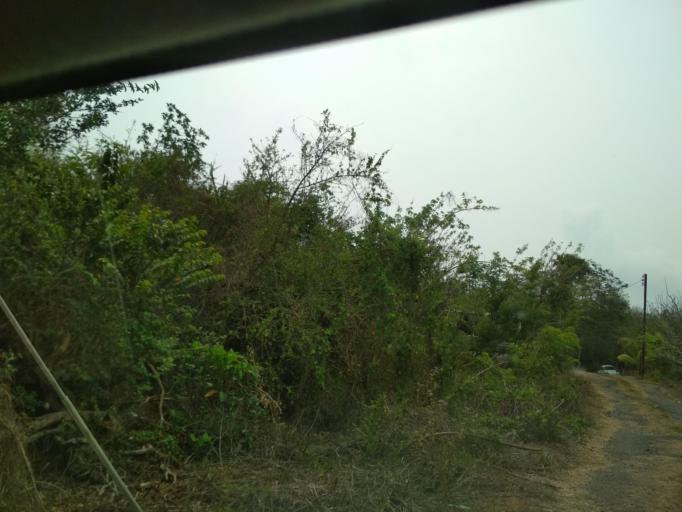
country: MX
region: Veracruz
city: Paso del Toro
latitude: 19.0249
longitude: -96.1401
